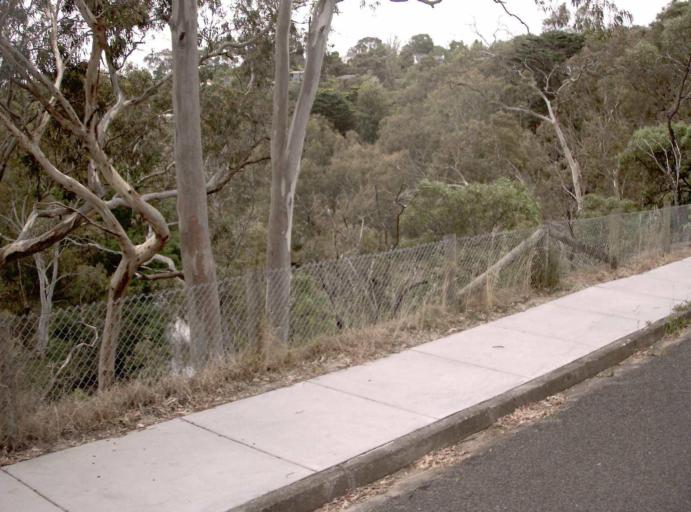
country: AU
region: Victoria
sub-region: Boroondara
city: Kew
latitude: -37.8036
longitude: 145.0209
